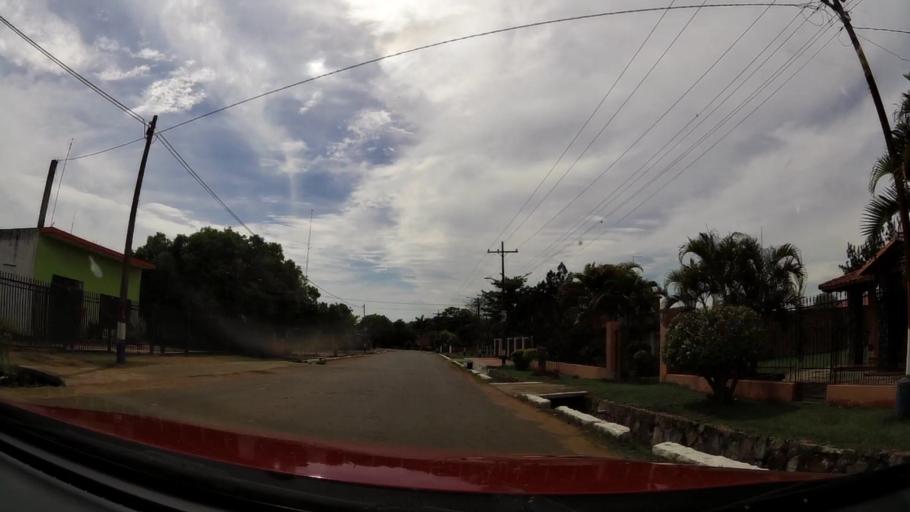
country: PY
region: Central
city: Limpio
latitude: -25.1811
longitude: -57.4458
